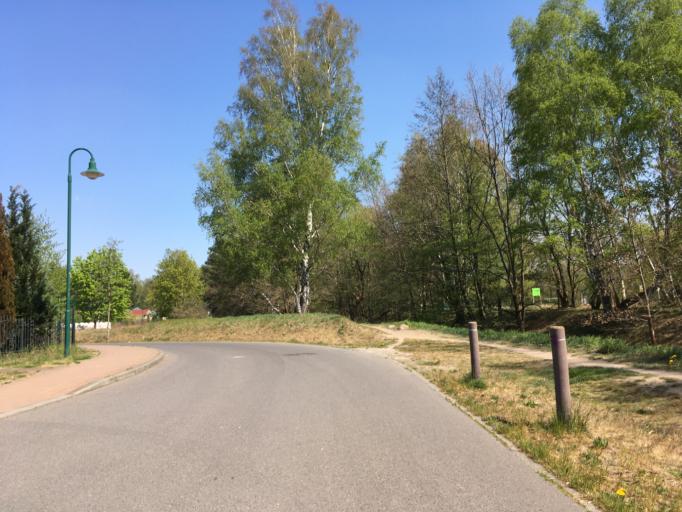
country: DE
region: Berlin
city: Buch
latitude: 52.6633
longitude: 13.5340
